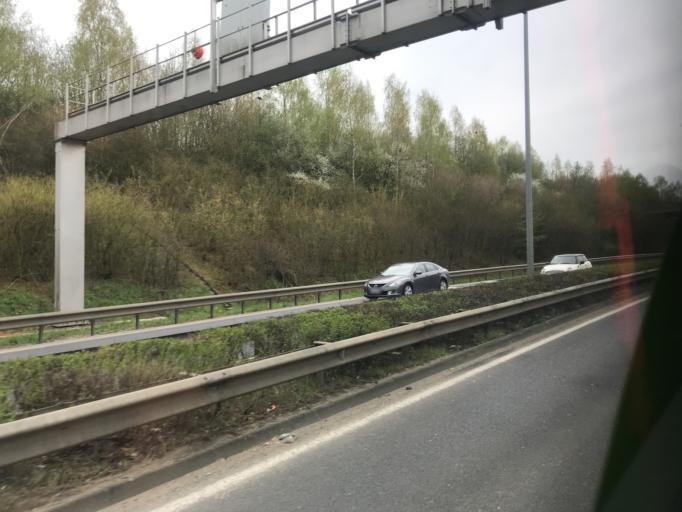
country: LU
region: Luxembourg
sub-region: Canton de Luxembourg
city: Hesperange
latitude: 49.5846
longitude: 6.1331
